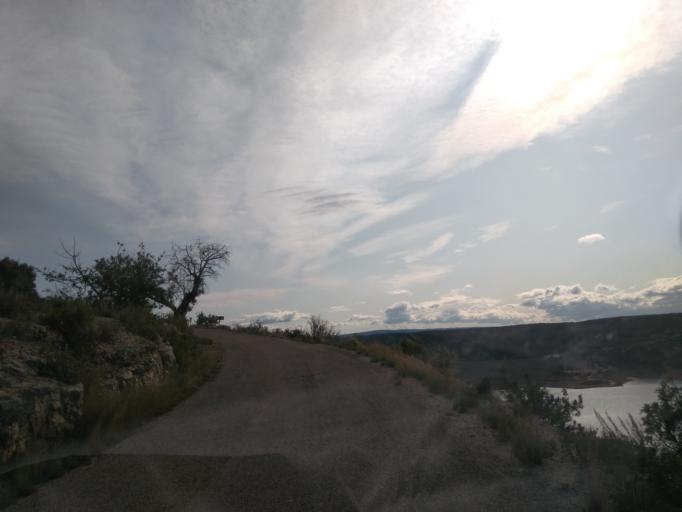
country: ES
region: Valencia
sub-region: Provincia de Valencia
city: Sumacarcer
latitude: 39.1474
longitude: -0.6474
